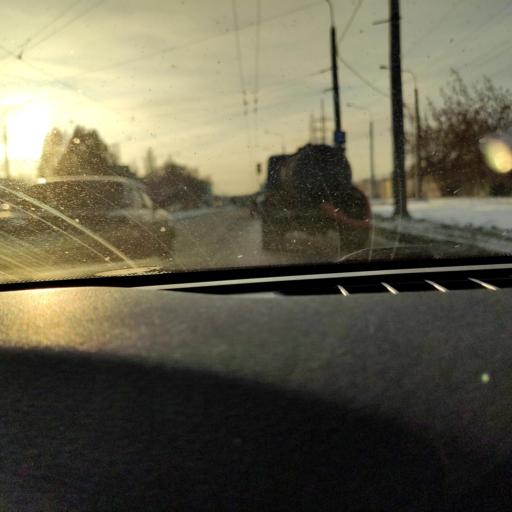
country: RU
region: Samara
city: Samara
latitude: 53.2035
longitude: 50.2667
